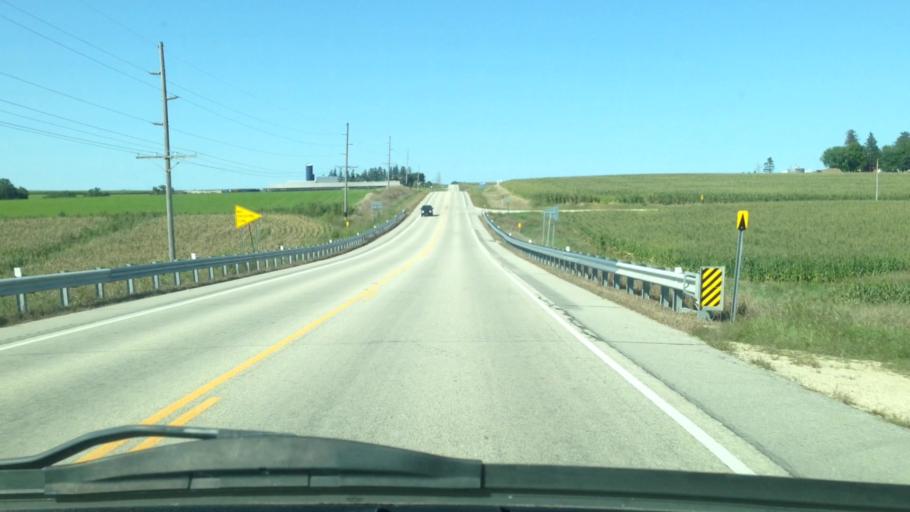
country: US
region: Minnesota
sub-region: Fillmore County
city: Rushford
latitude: 43.8885
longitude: -91.7398
